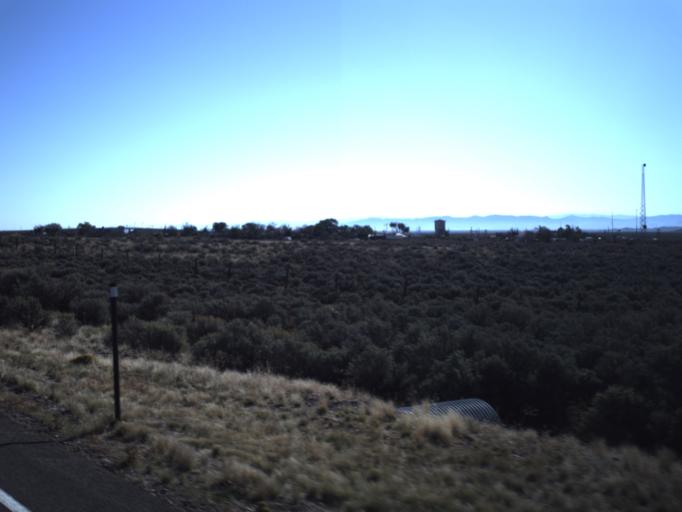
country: US
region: Utah
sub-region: Washington County
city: Enterprise
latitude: 37.7991
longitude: -113.9330
